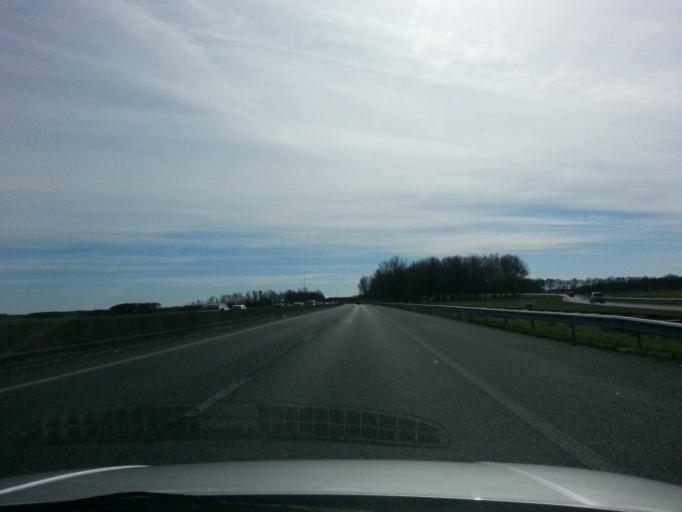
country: NL
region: Drenthe
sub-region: Gemeente Tynaarlo
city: Tynaarlo
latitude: 53.1163
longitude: 6.6107
